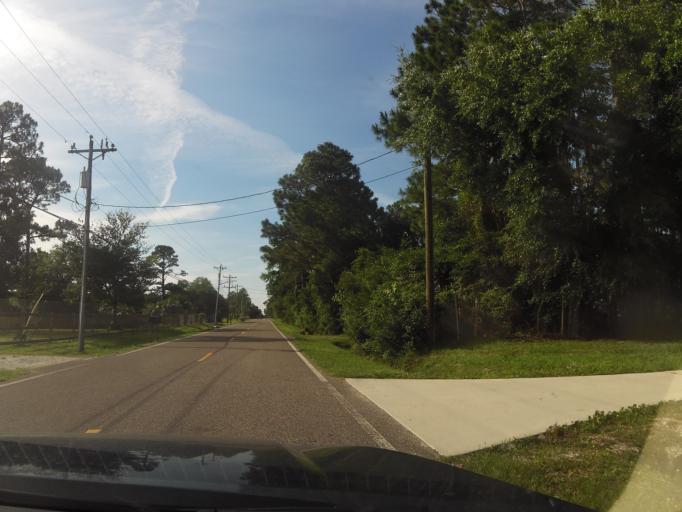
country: US
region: Florida
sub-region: Nassau County
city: Fernandina Beach
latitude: 30.5116
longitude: -81.4766
